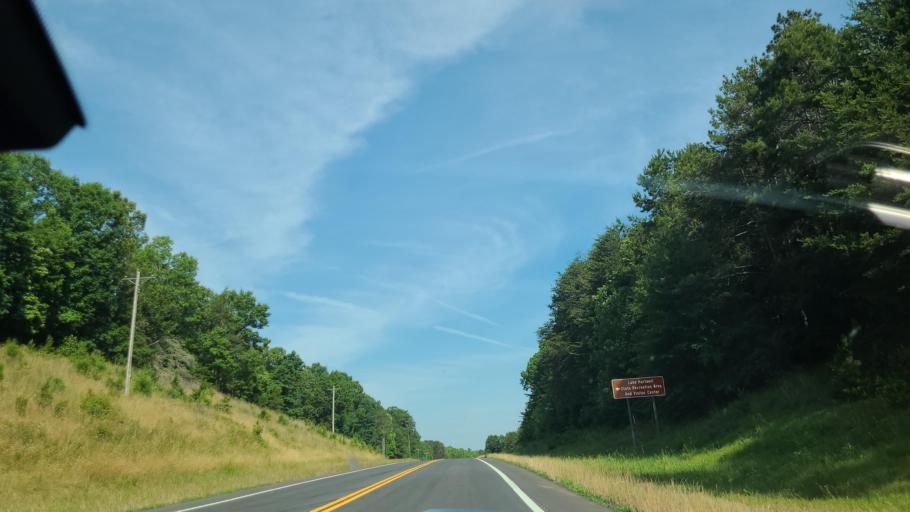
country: US
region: Georgia
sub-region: Franklin County
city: Gumlog
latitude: 34.4939
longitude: -83.0293
